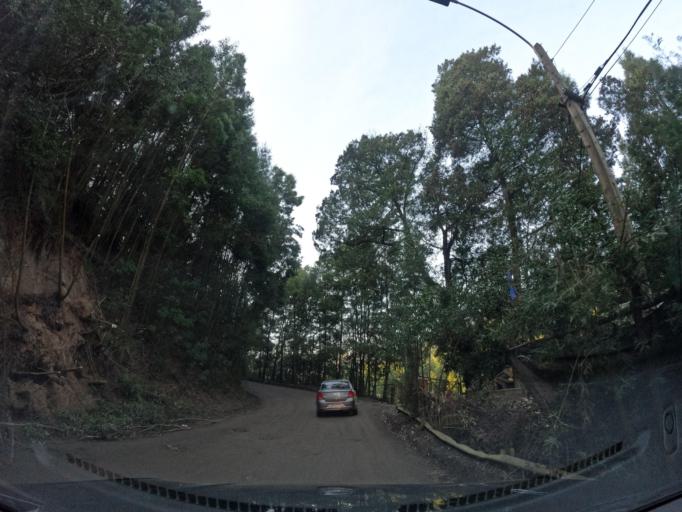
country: CL
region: Biobio
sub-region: Provincia de Concepcion
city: Concepcion
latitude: -36.8473
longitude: -73.0082
